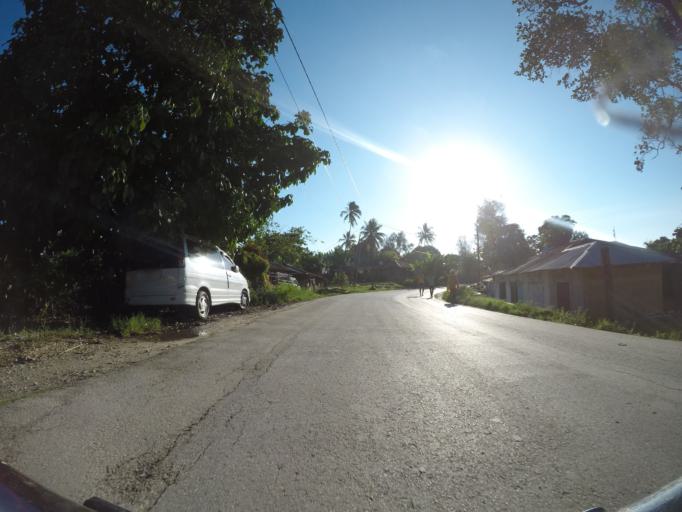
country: TZ
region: Pemba South
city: Mtambile
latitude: -5.3790
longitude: 39.7000
